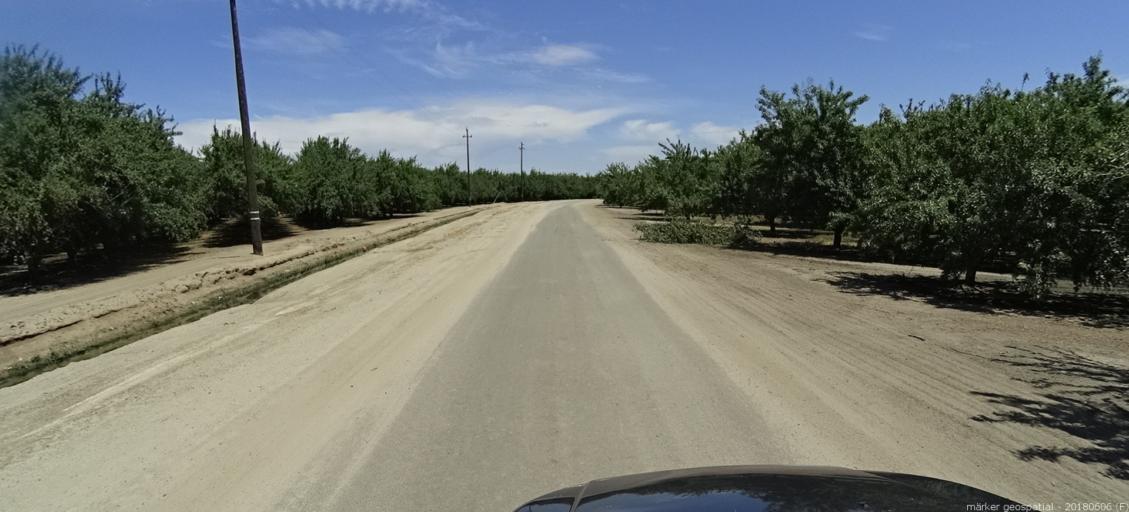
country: US
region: California
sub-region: Fresno County
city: Mendota
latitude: 36.8025
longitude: -120.3535
